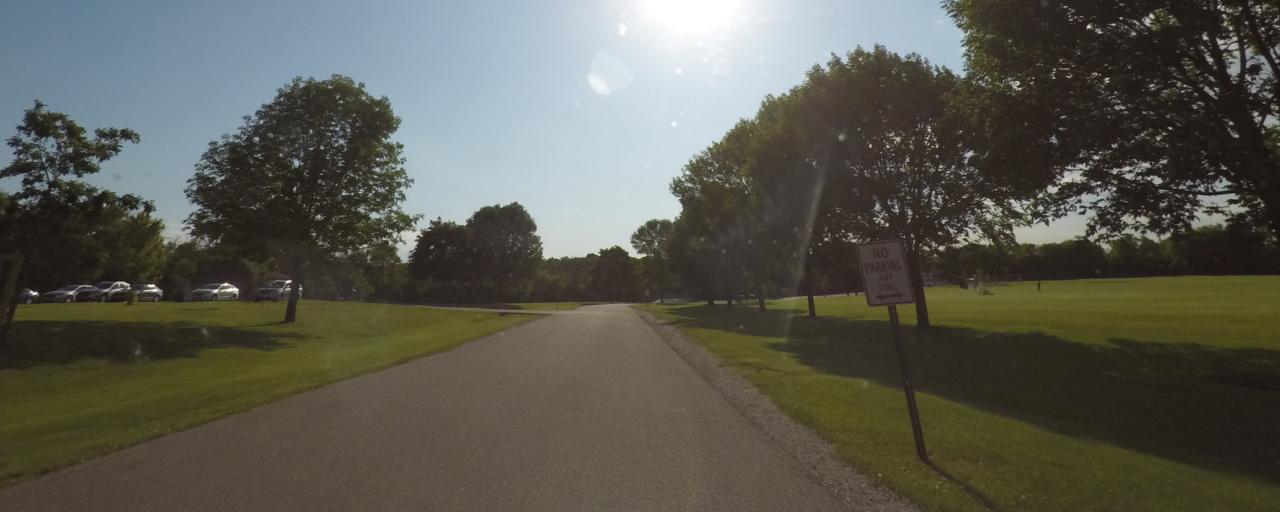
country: US
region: Wisconsin
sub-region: Waukesha County
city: New Berlin
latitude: 42.9523
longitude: -88.0910
